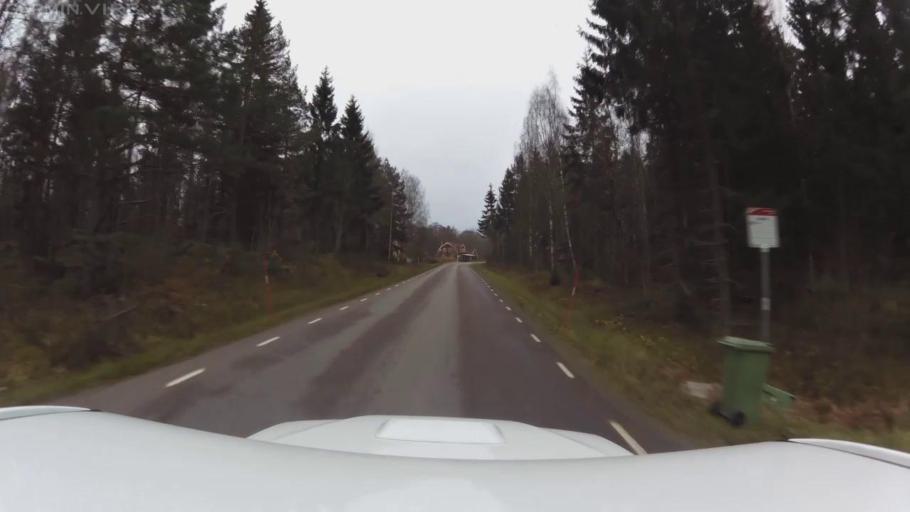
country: SE
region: OEstergoetland
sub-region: Linkopings Kommun
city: Vikingstad
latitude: 58.2335
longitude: 15.3929
